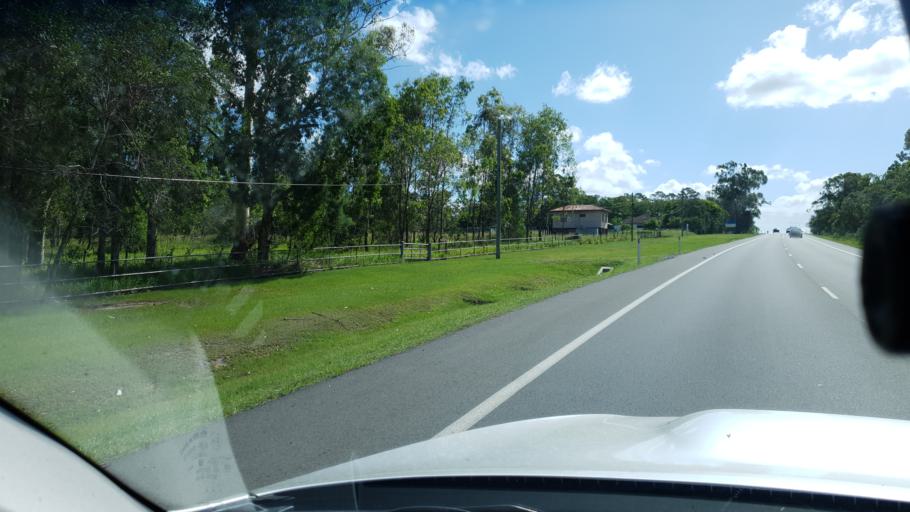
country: AU
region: Queensland
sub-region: Logan
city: Woodridge
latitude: -27.6499
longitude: 153.0837
